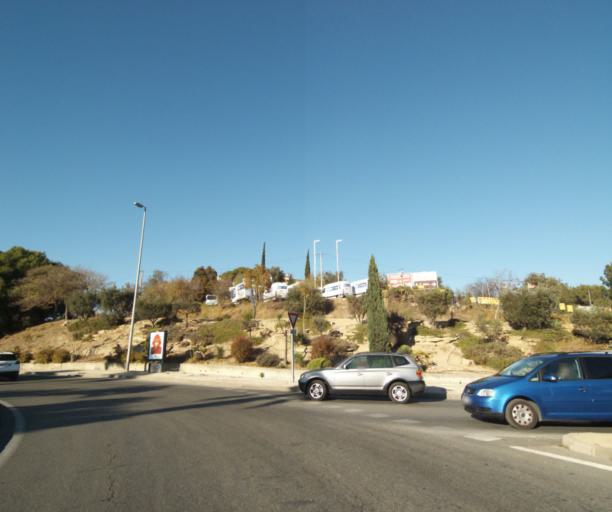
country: FR
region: Provence-Alpes-Cote d'Azur
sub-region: Departement des Bouches-du-Rhone
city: La Ciotat
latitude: 43.1919
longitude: 5.6049
